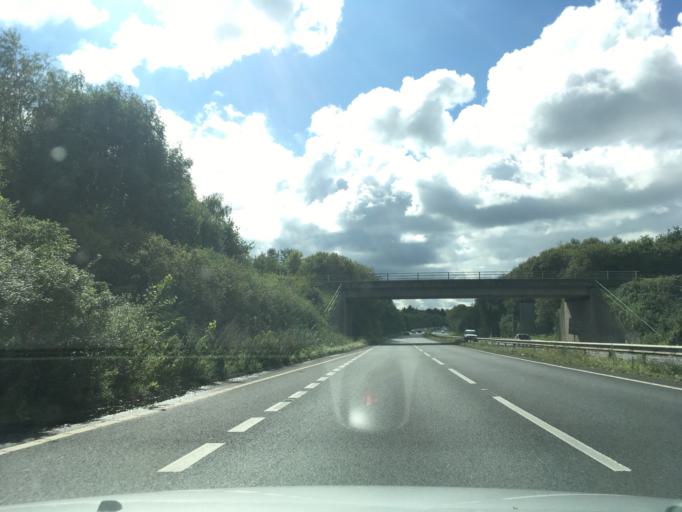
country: GB
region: England
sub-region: Hampshire
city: Liss
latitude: 51.0367
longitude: -0.9049
